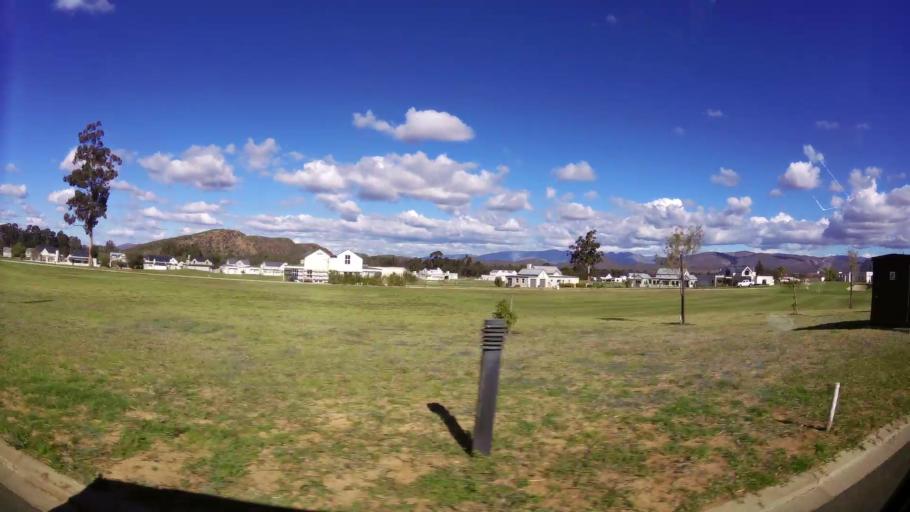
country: ZA
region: Western Cape
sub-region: Cape Winelands District Municipality
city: Ashton
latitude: -33.8136
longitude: 19.8463
